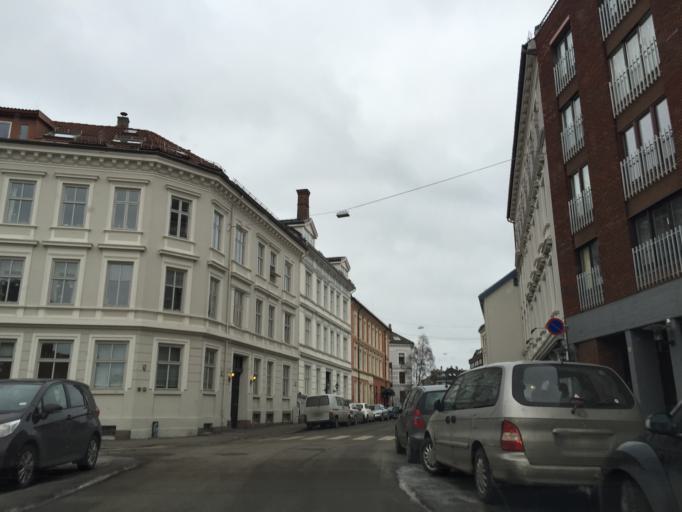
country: NO
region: Oslo
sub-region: Oslo
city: Oslo
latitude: 59.9219
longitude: 10.7159
